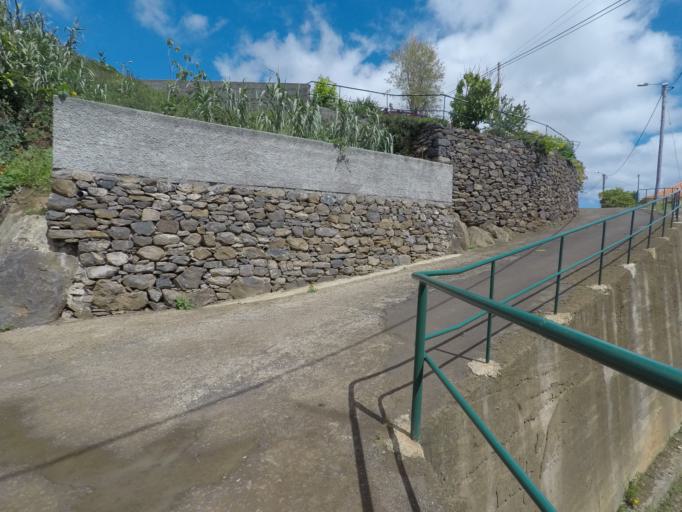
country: PT
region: Madeira
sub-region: Calheta
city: Estreito da Calheta
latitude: 32.7357
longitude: -17.1848
